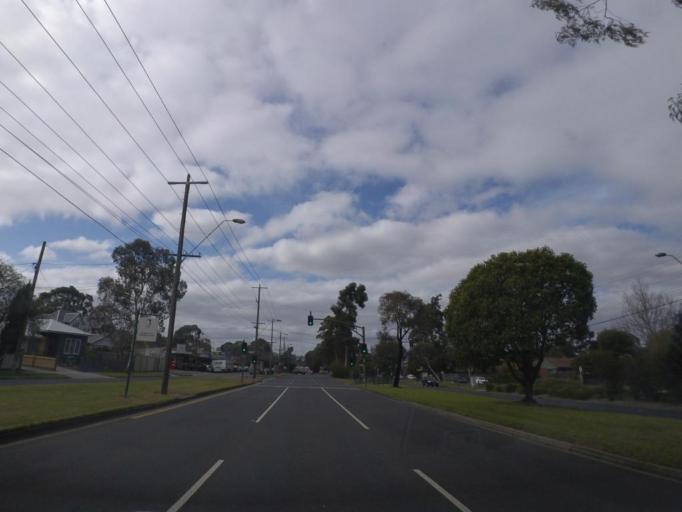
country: AU
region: Victoria
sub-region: Whitehorse
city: Vermont
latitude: -37.8337
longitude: 145.2068
